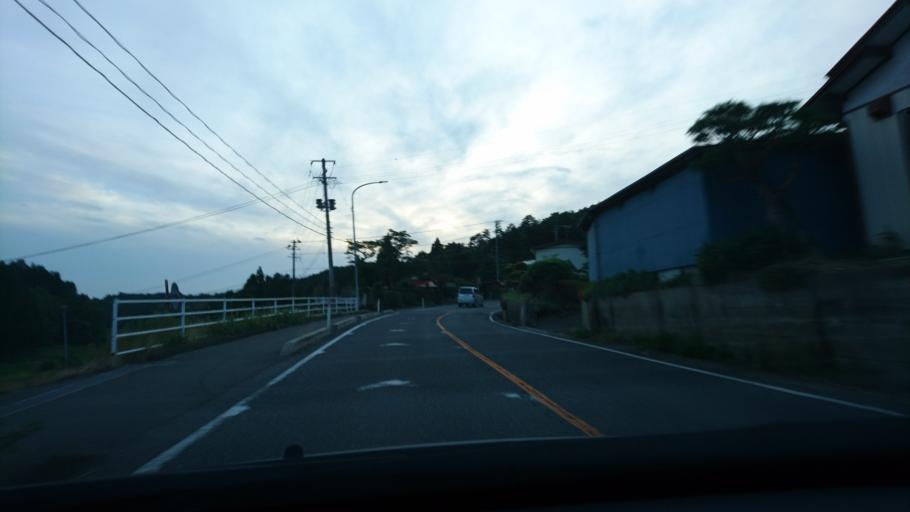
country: JP
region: Miyagi
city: Furukawa
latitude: 38.7544
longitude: 141.0080
